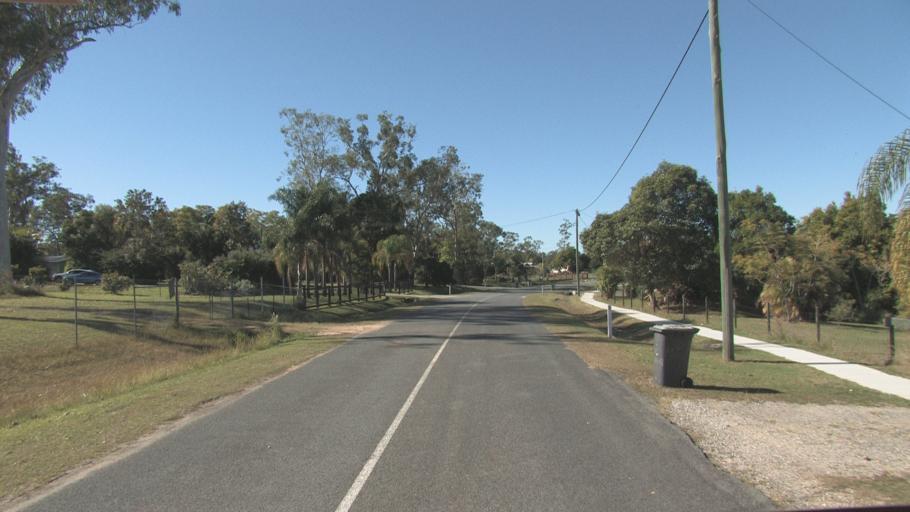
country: AU
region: Queensland
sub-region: Logan
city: Park Ridge South
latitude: -27.7330
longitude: 153.0433
